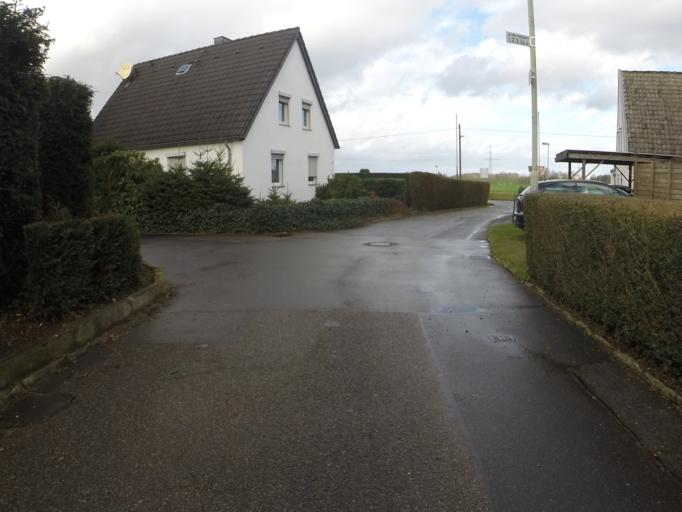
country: NL
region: Limburg
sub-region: Gemeente Kerkrade
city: Kerkrade
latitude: 50.8274
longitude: 6.0664
